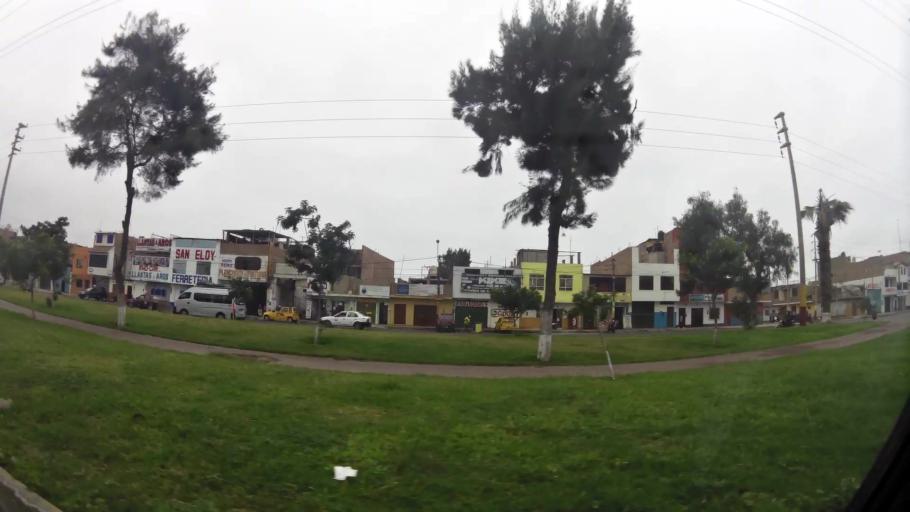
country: PE
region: Ancash
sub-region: Provincia de Santa
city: Chimbote
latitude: -9.0788
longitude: -78.5803
